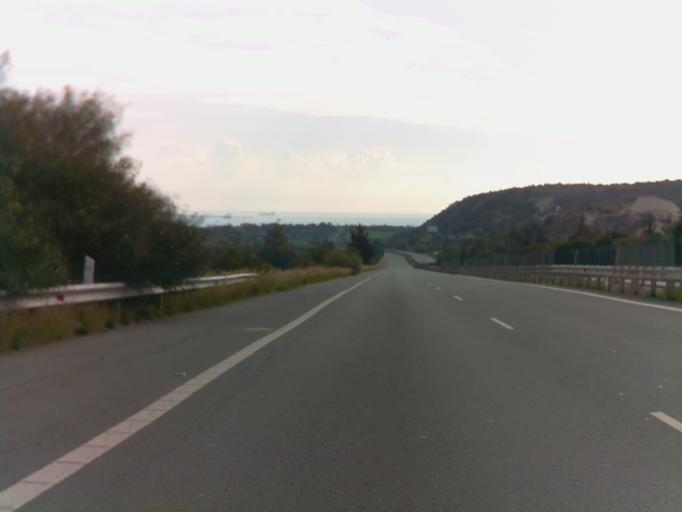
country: CY
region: Limassol
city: Pyrgos
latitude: 34.7234
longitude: 33.2513
